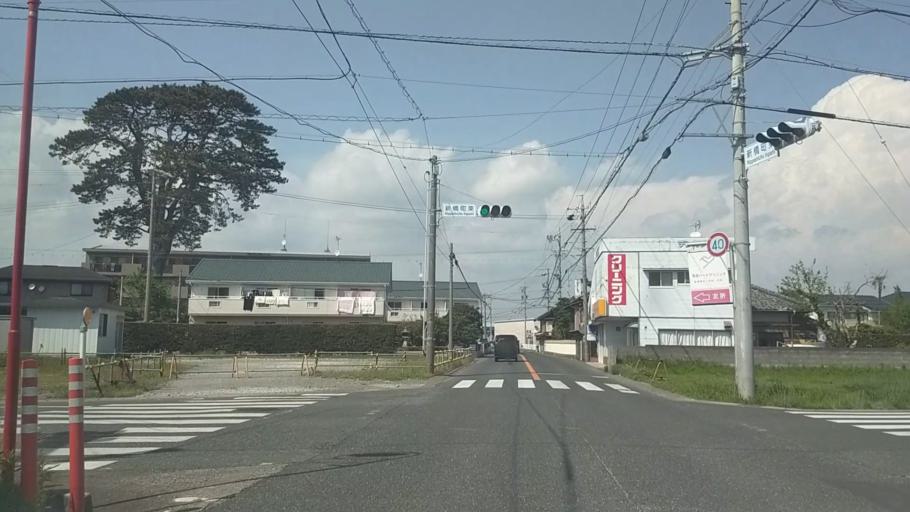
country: JP
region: Shizuoka
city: Hamamatsu
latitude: 34.6818
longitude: 137.7100
